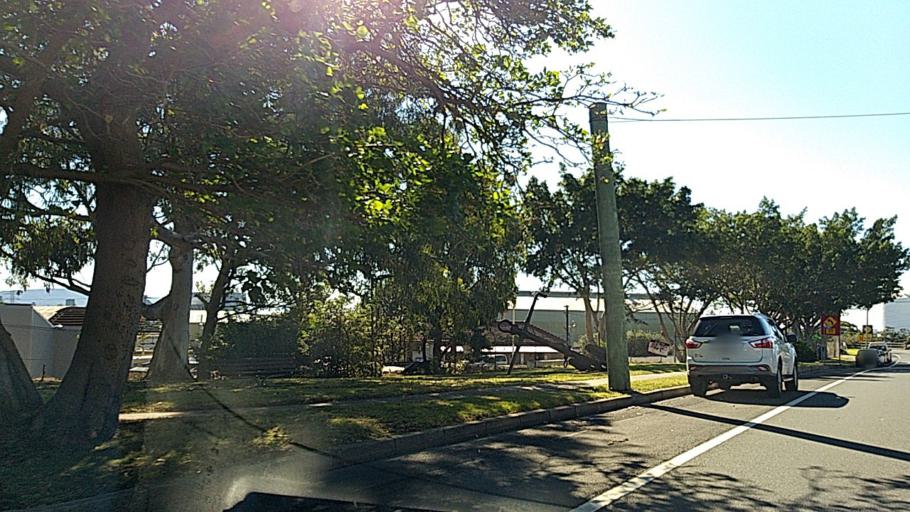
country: AU
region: New South Wales
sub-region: Wollongong
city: Port Kembla
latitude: -34.4790
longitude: 150.9025
